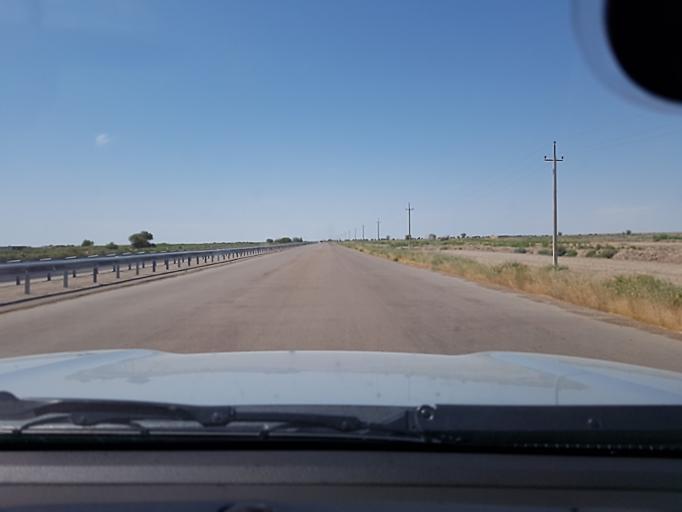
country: TM
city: Akdepe
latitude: 41.7366
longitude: 59.1123
